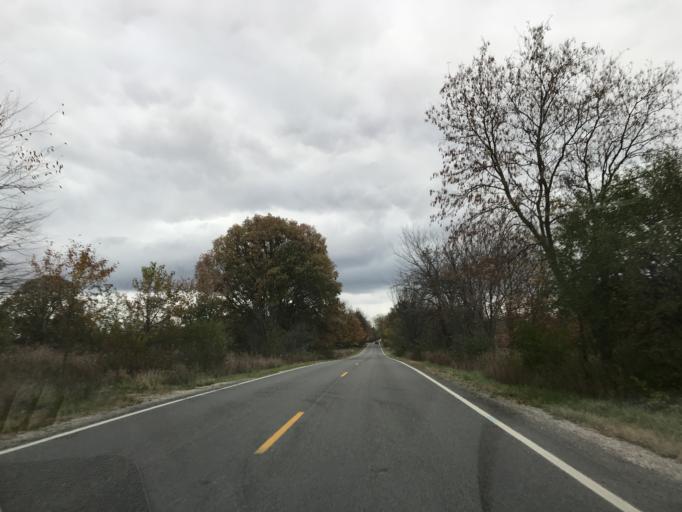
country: US
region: Michigan
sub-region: Washtenaw County
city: Ann Arbor
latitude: 42.3371
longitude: -83.7208
